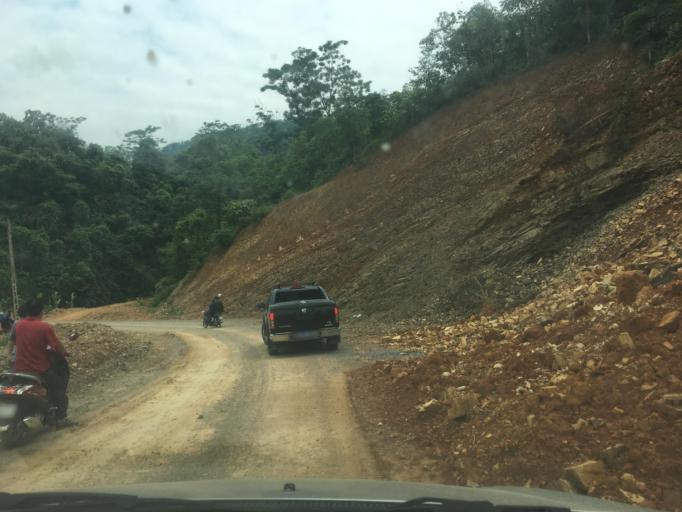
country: VN
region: Lang Son
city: Binh Gia
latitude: 22.1340
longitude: 106.3403
